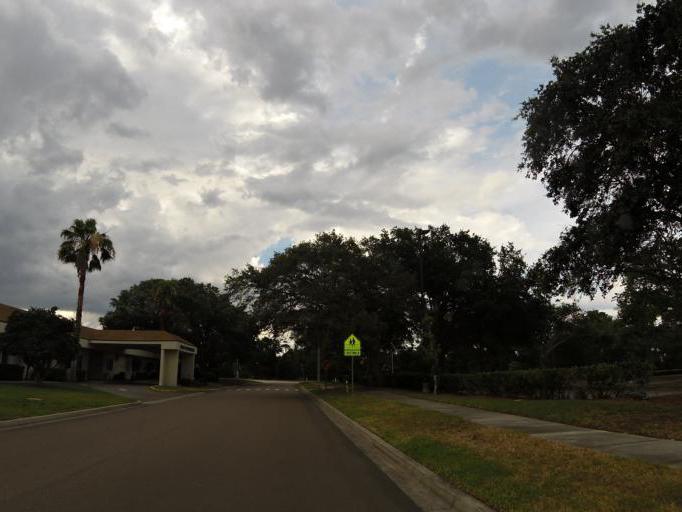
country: US
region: Florida
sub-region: Duval County
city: Jacksonville Beach
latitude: 30.2735
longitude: -81.4006
